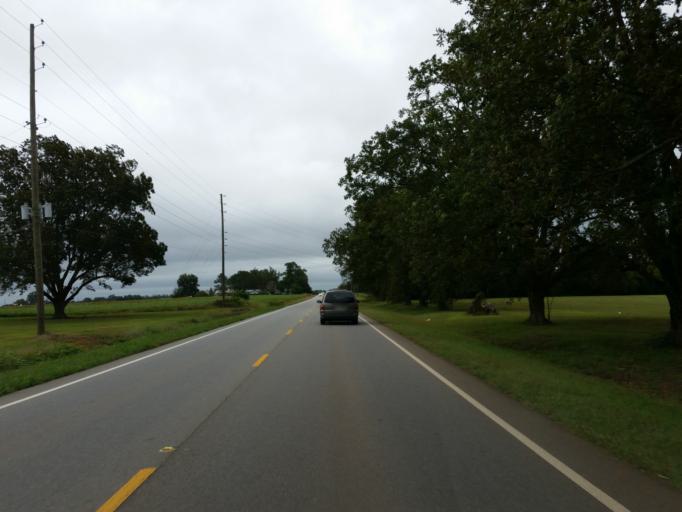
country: US
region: Georgia
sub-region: Peach County
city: Fort Valley
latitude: 32.5828
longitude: -83.9210
